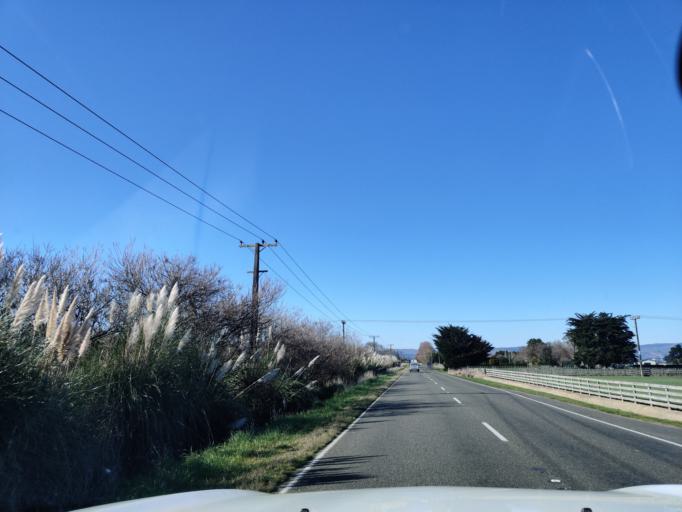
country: NZ
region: Manawatu-Wanganui
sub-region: Palmerston North City
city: Palmerston North
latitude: -40.3122
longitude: 175.5924
